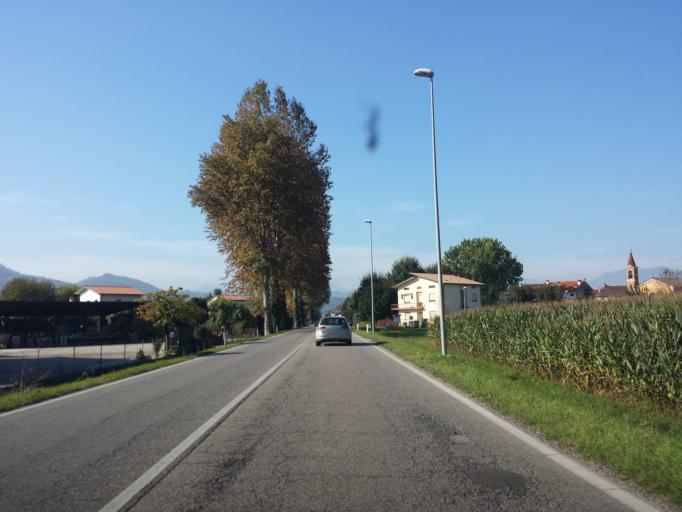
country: IT
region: Veneto
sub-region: Provincia di Vicenza
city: Motta
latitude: 45.6067
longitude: 11.4861
